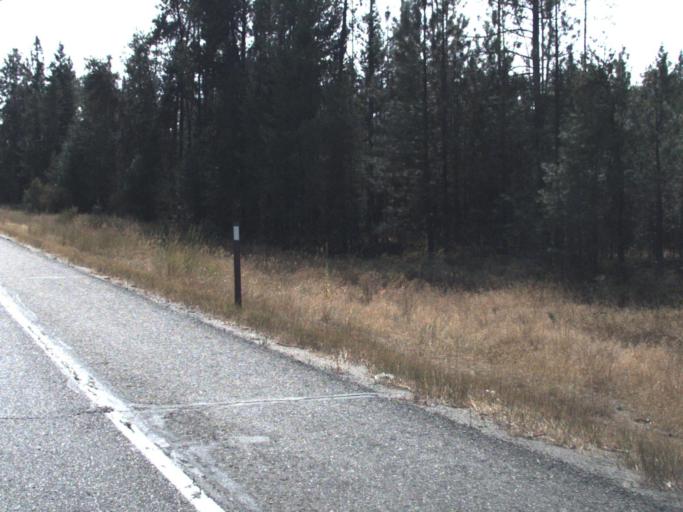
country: US
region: Washington
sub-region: Spokane County
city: Deer Park
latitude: 48.0752
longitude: -117.6278
